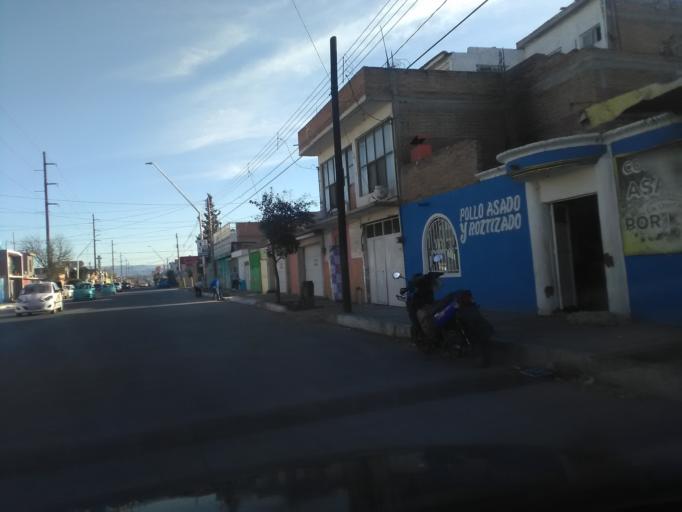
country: MX
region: Durango
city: Victoria de Durango
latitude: 24.0238
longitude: -104.6331
